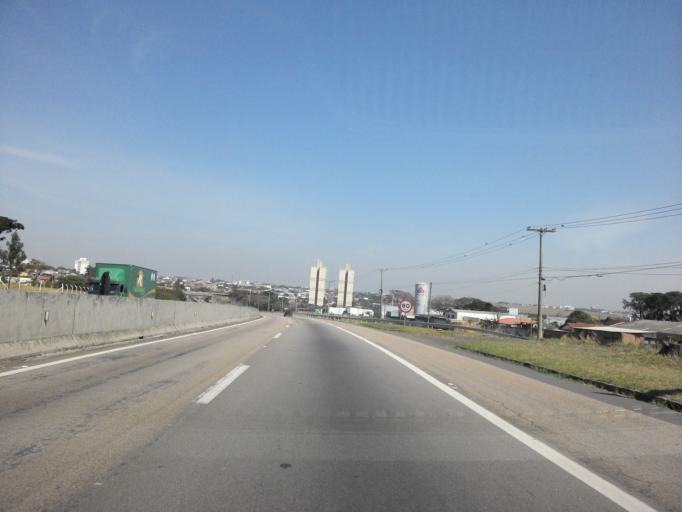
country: BR
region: Sao Paulo
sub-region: Hortolandia
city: Hortolandia
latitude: -22.8861
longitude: -47.1592
